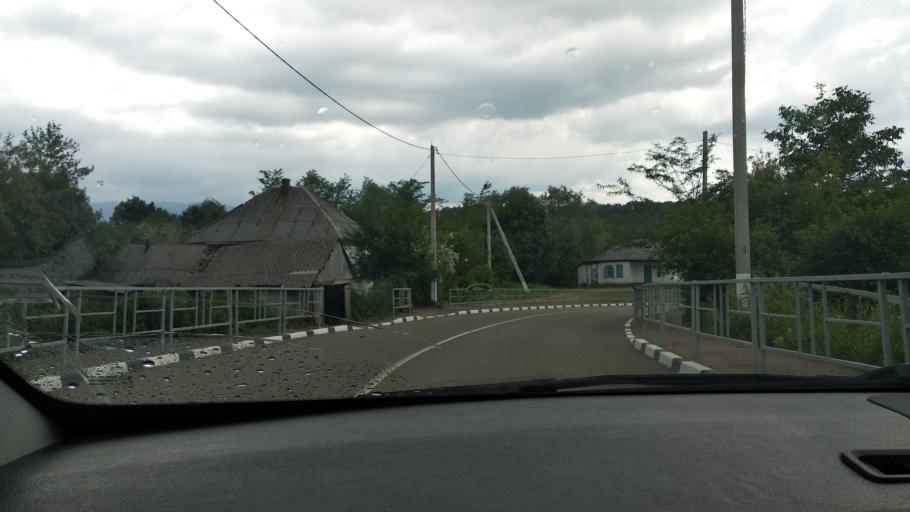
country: RU
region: Krasnodarskiy
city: Neftegorsk
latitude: 44.2717
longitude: 39.9243
